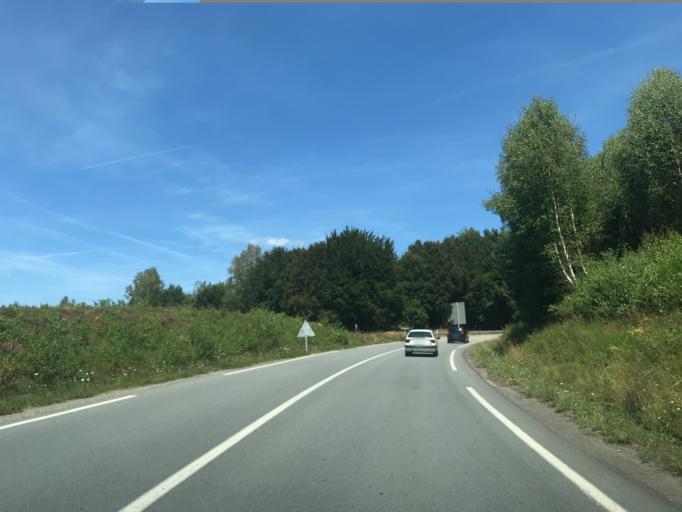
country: FR
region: Limousin
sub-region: Departement de la Correze
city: Egletons
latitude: 45.3939
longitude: 2.0314
